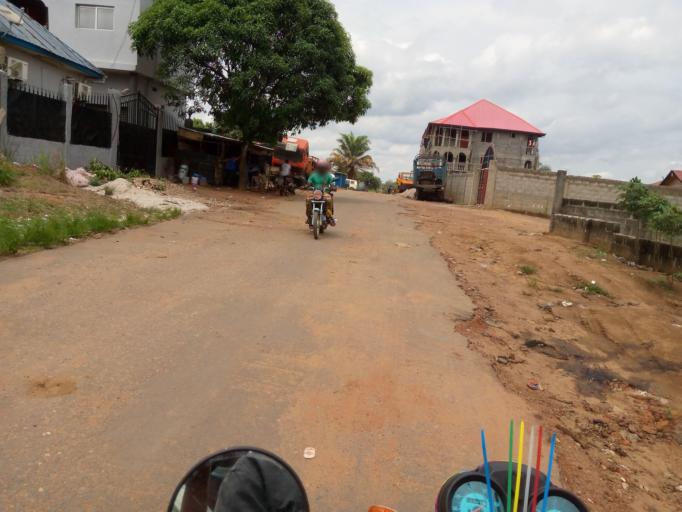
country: SL
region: Western Area
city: Waterloo
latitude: 8.3348
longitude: -13.0311
